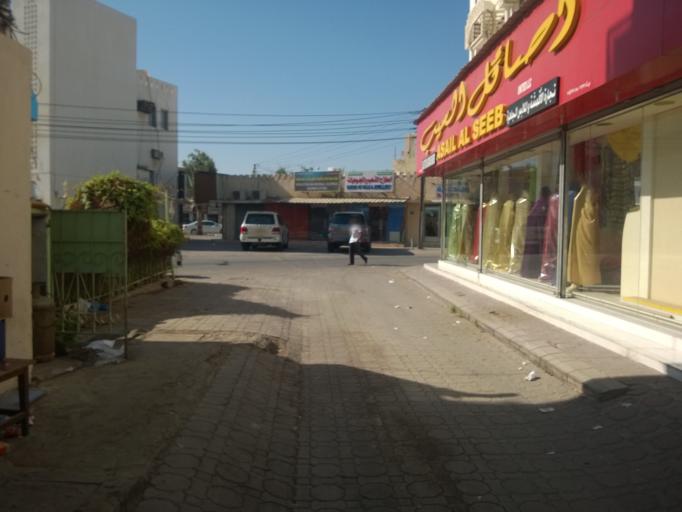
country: OM
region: Muhafazat Masqat
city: As Sib al Jadidah
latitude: 23.6774
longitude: 58.1904
